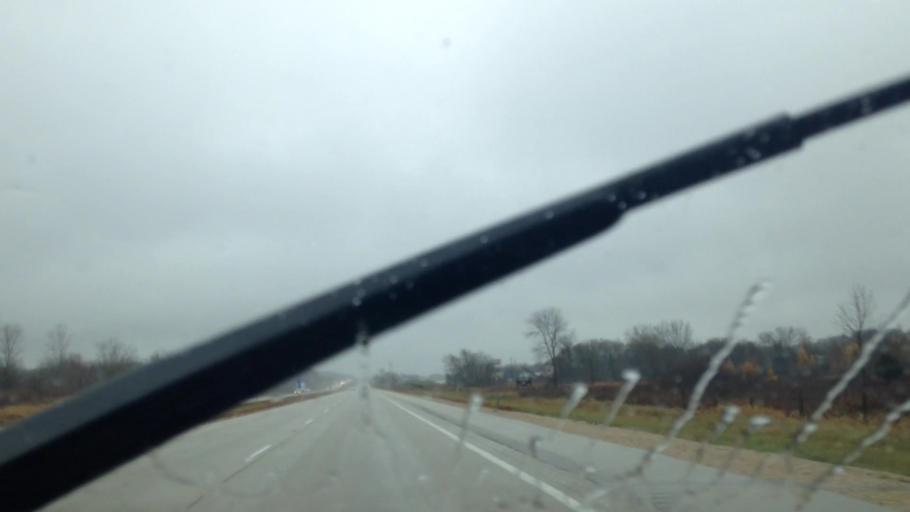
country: US
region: Wisconsin
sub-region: Washington County
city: Slinger
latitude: 43.3868
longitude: -88.3112
